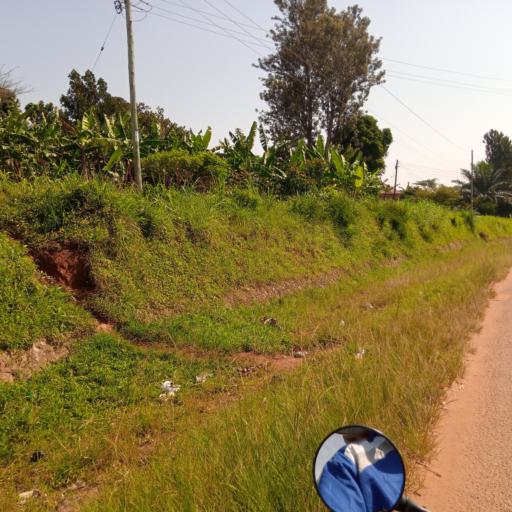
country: UG
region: Central Region
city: Masaka
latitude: -0.3644
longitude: 31.7175
